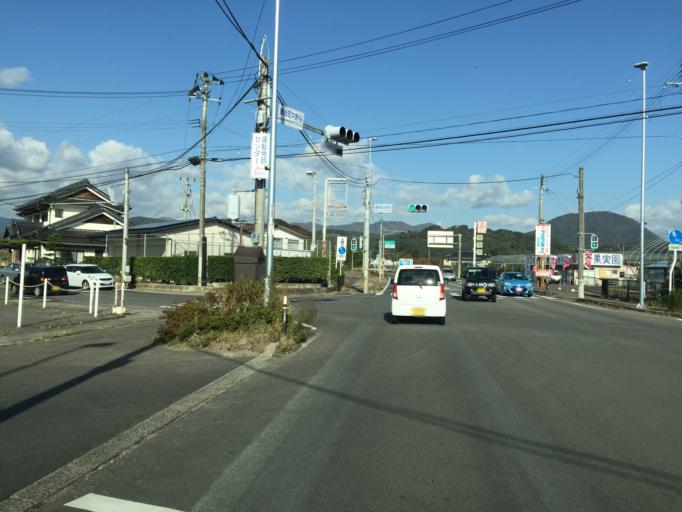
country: JP
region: Fukushima
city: Fukushima-shi
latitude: 37.8180
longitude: 140.4364
